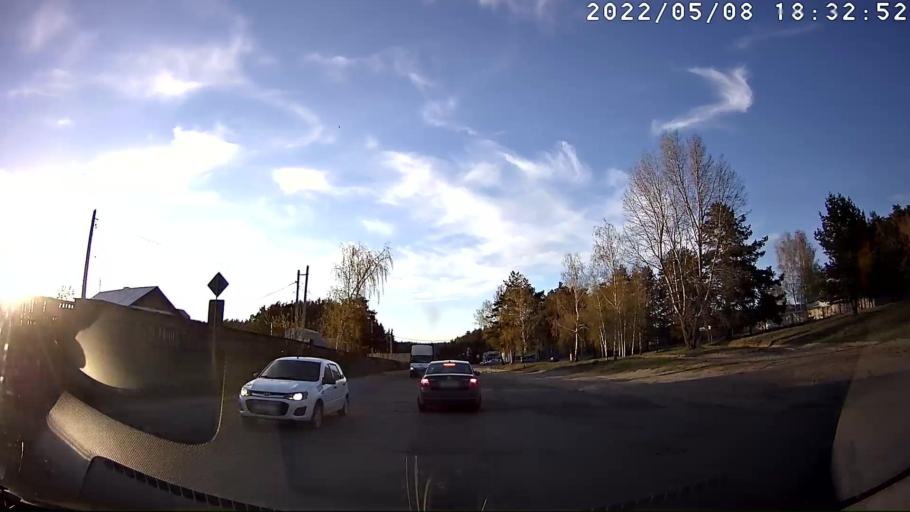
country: RU
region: Mariy-El
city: Volzhsk
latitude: 55.8873
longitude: 48.3593
